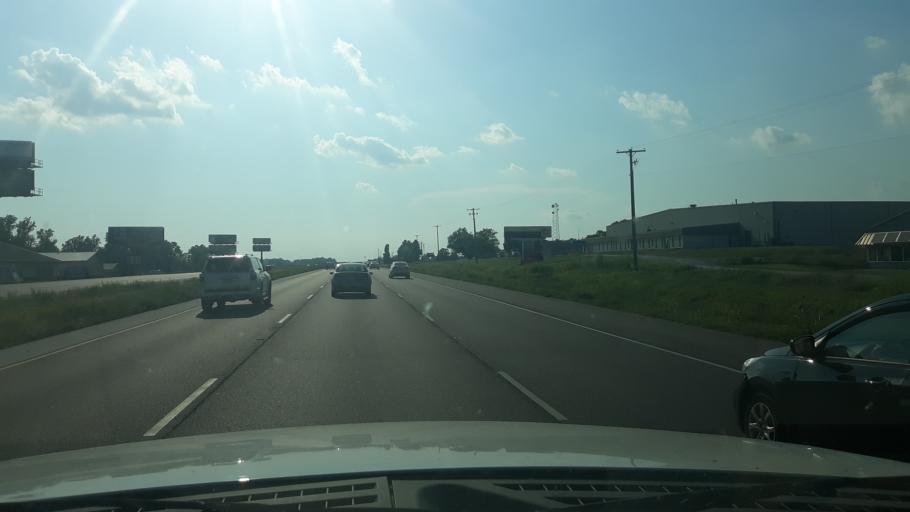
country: US
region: Illinois
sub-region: Williamson County
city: Crainville
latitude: 37.7450
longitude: -89.0459
